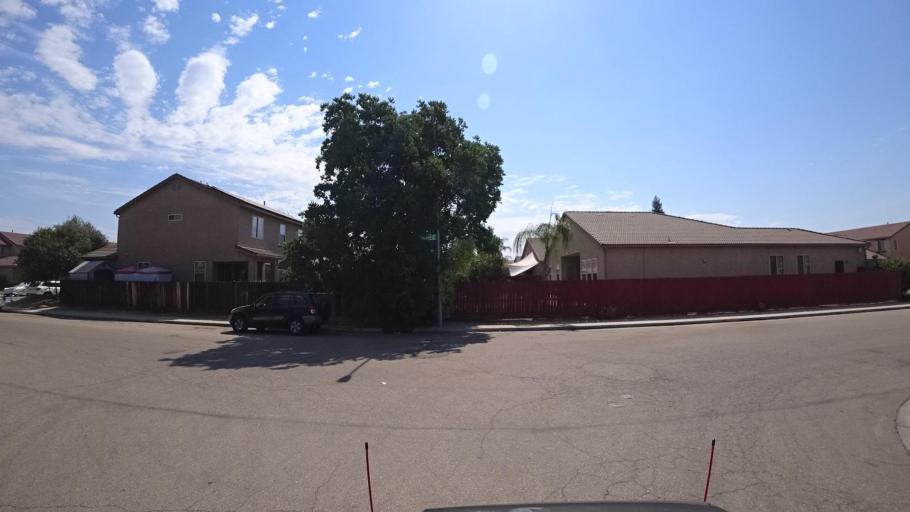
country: US
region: California
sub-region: Fresno County
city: Sunnyside
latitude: 36.7200
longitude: -119.6885
